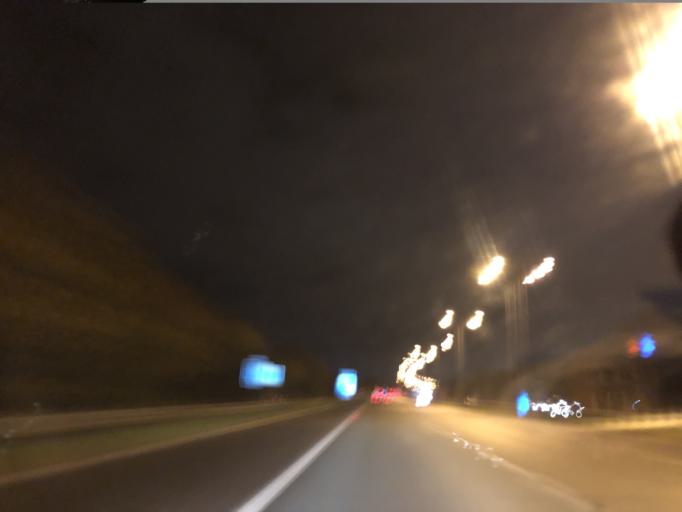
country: GB
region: England
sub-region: Kirklees
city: Cleckheaton
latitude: 53.7470
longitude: -1.7363
